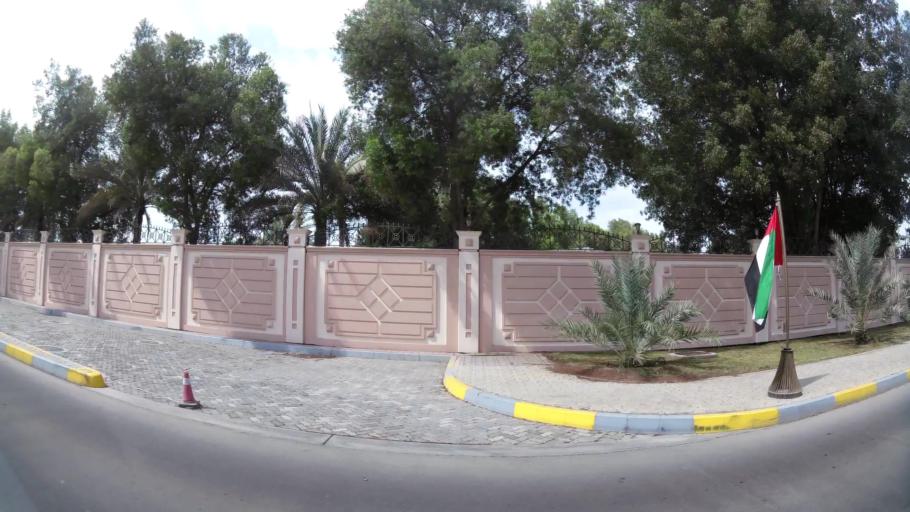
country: AE
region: Abu Dhabi
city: Abu Dhabi
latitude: 24.4493
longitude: 54.3470
